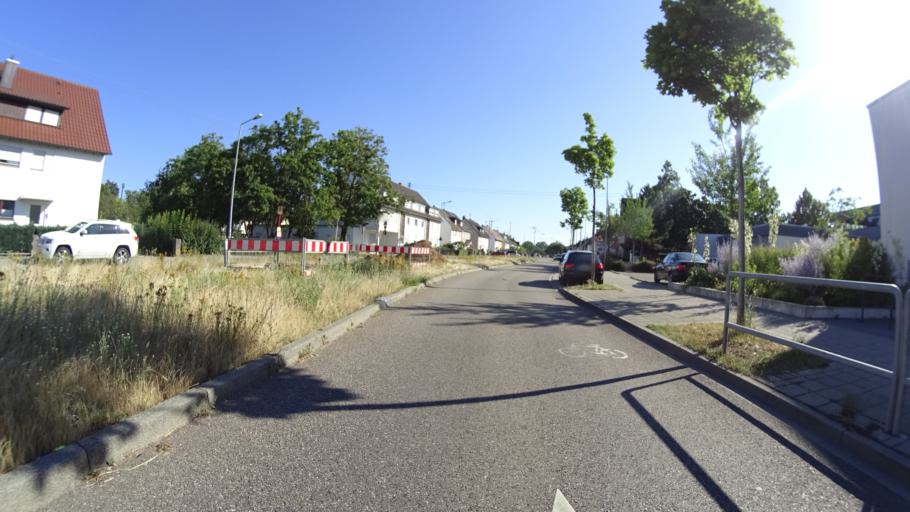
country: DE
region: Baden-Wuerttemberg
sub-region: Karlsruhe Region
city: Karlsruhe
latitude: 49.0328
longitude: 8.3471
